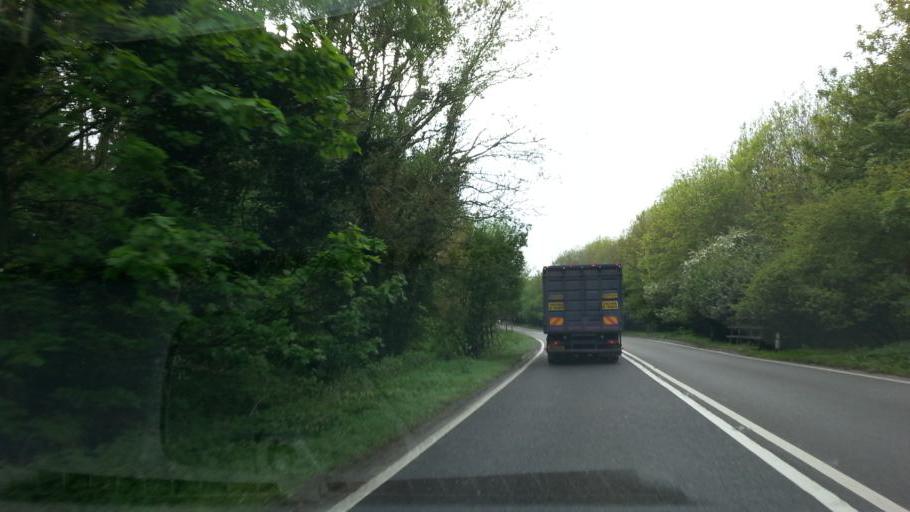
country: GB
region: England
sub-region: Nottinghamshire
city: South Collingham
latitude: 53.0793
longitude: -0.7098
